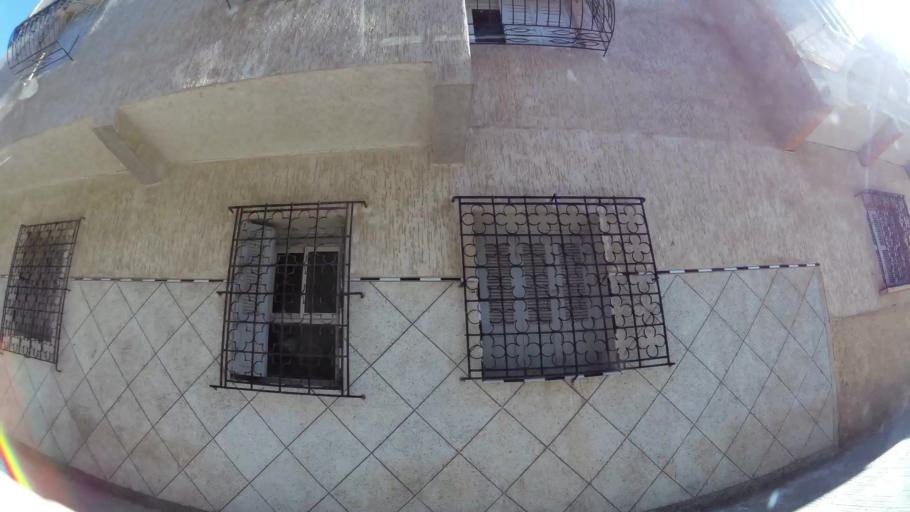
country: MA
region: Meknes-Tafilalet
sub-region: Meknes
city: Meknes
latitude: 33.8928
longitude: -5.5067
